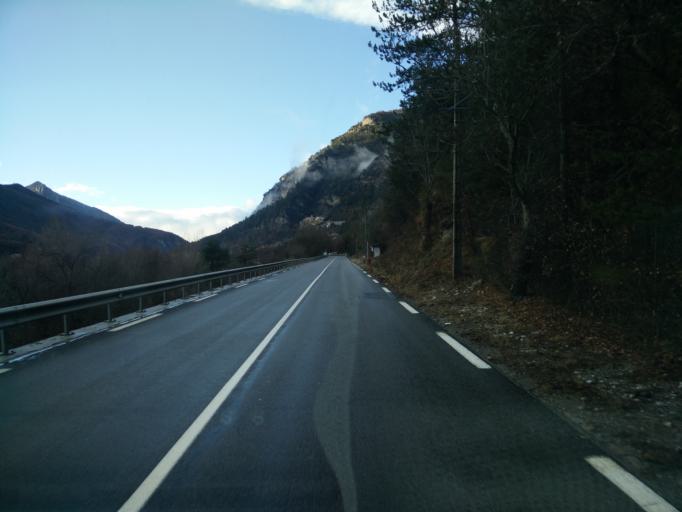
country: FR
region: Provence-Alpes-Cote d'Azur
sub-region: Departement des Alpes-Maritimes
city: Puget-Theniers
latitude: 43.9457
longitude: 7.0221
